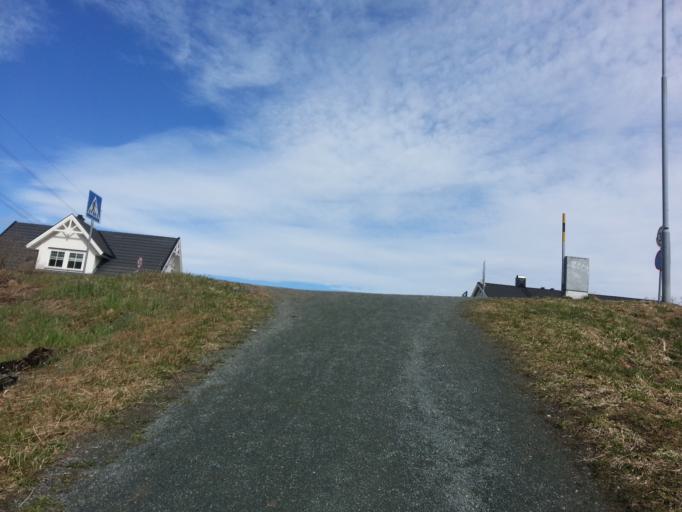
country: NO
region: Sor-Trondelag
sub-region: Trondheim
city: Trondheim
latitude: 63.4183
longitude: 10.4429
